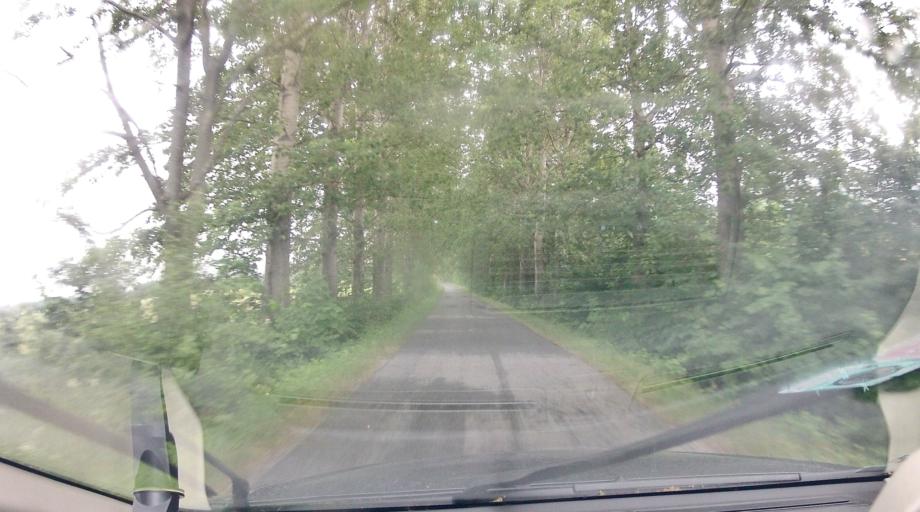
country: PL
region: Lower Silesian Voivodeship
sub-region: Powiat klodzki
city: Miedzylesie
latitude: 50.1780
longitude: 16.7166
